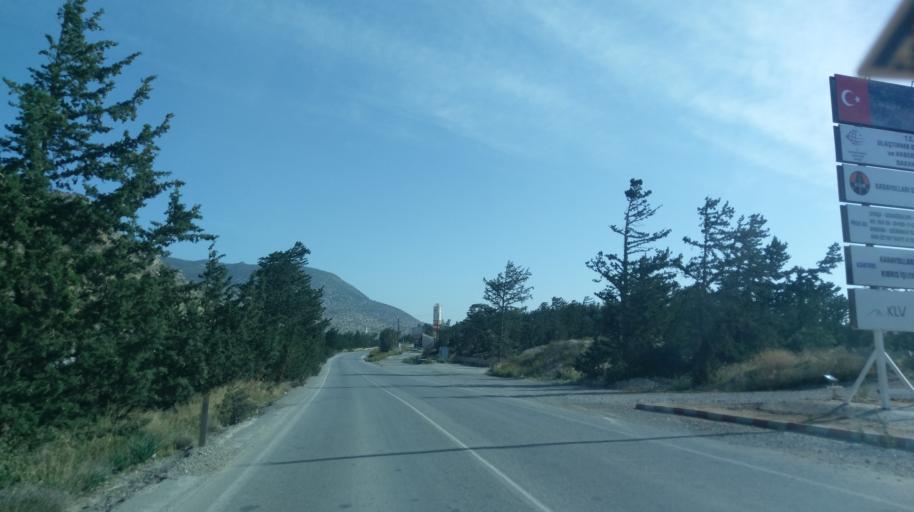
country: CY
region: Lefkosia
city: Nicosia
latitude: 35.2681
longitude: 33.4676
